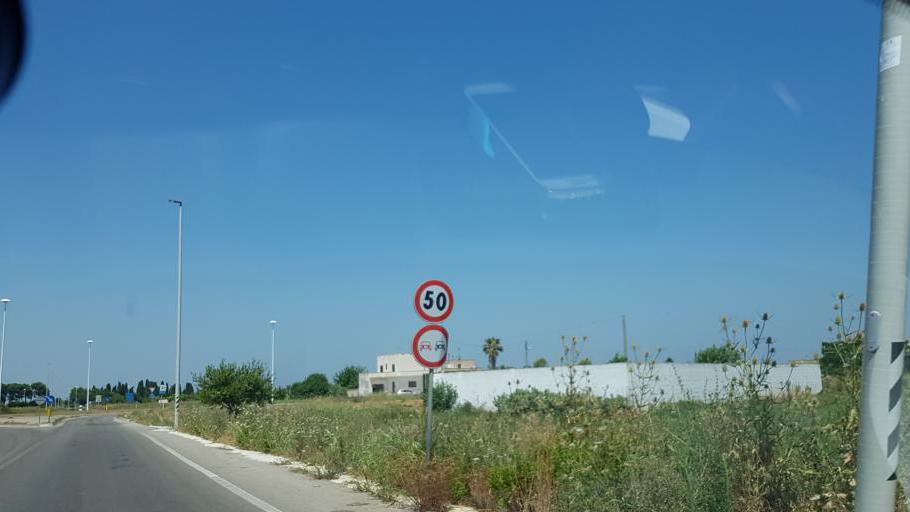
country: IT
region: Apulia
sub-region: Provincia di Lecce
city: Salice Salentino
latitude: 40.3794
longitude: 17.9698
